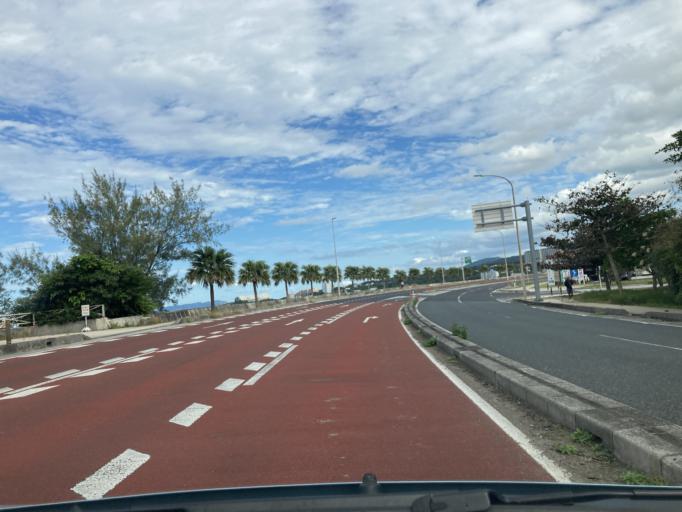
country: JP
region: Okinawa
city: Ishikawa
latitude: 26.4366
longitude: 127.7911
